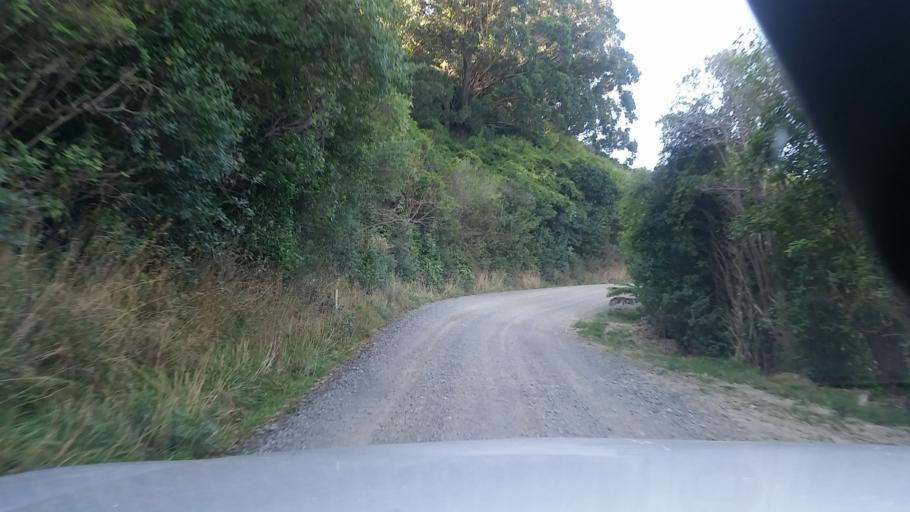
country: NZ
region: Marlborough
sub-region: Marlborough District
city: Picton
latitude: -41.2962
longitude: 174.1174
